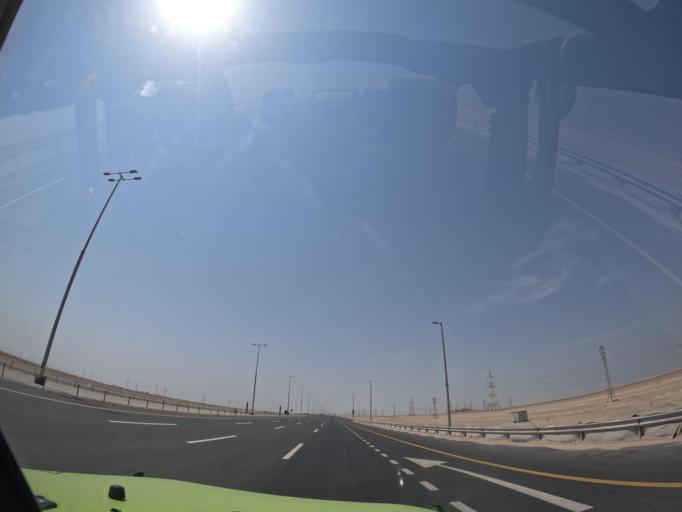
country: AE
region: Abu Dhabi
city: Abu Dhabi
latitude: 24.1566
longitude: 54.3203
